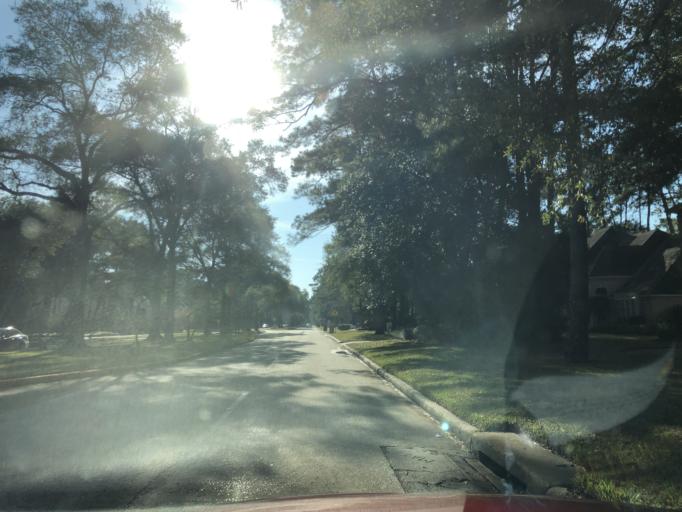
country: US
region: Texas
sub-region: Harris County
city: Tomball
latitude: 30.0230
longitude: -95.5483
